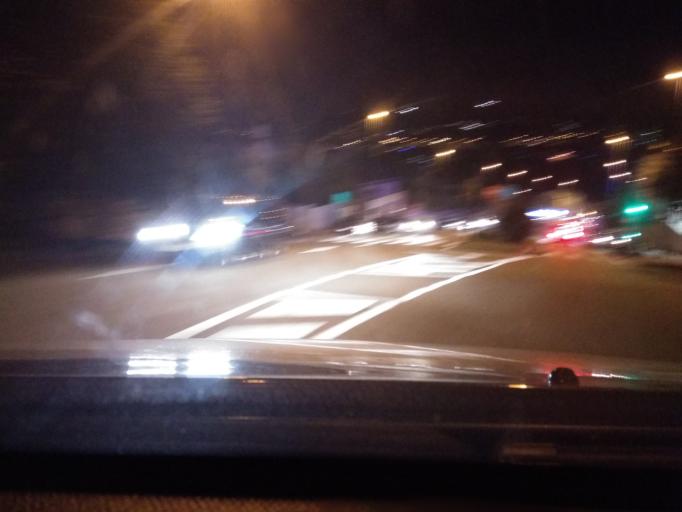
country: ES
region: Galicia
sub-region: Provincia de Pontevedra
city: Vigo
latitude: 42.2221
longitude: -8.7237
